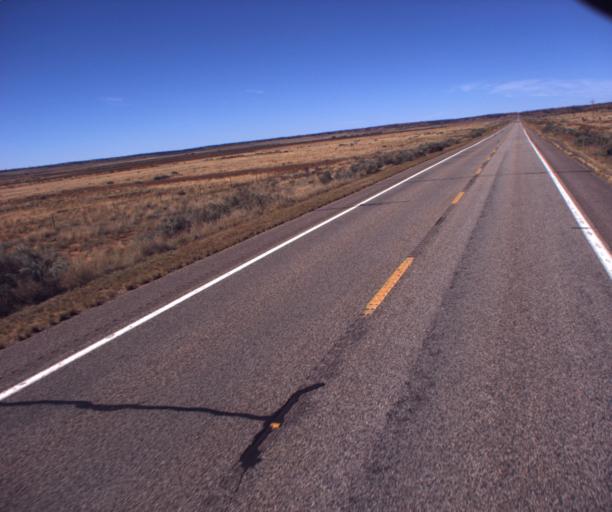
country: US
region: Arizona
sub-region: Mohave County
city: Colorado City
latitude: 36.8637
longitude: -112.8289
